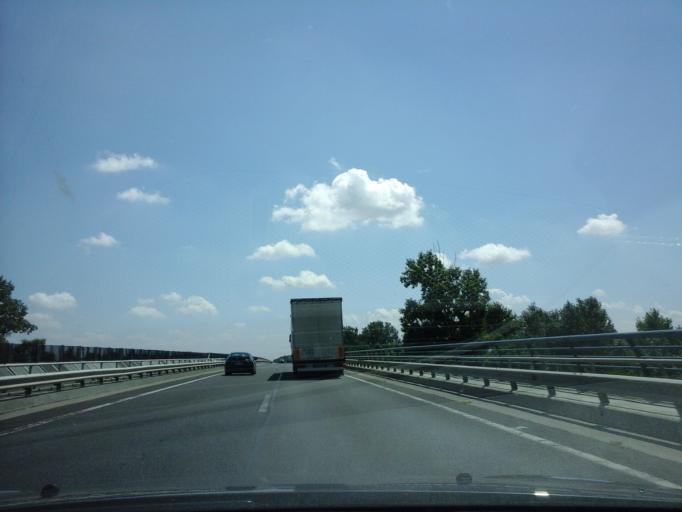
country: HU
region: Hajdu-Bihar
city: Polgar
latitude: 47.8571
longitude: 21.0519
